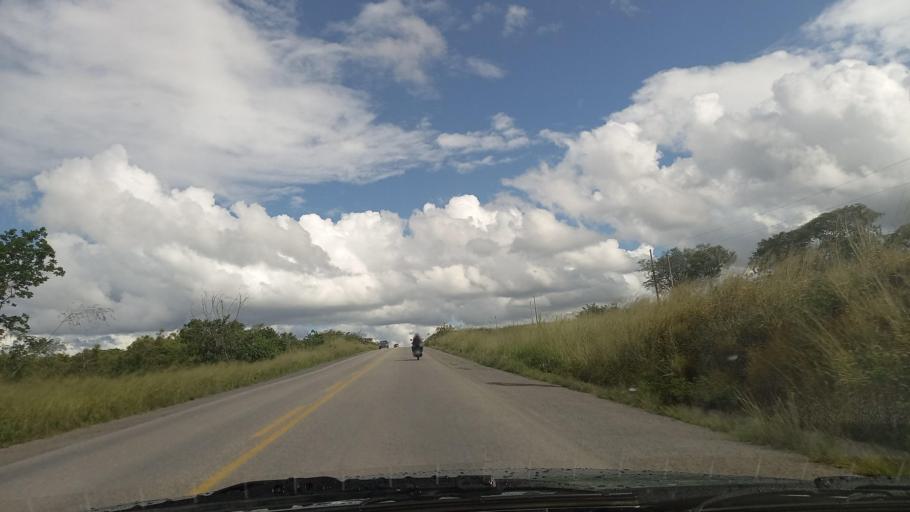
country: BR
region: Pernambuco
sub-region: Lajedo
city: Lajedo
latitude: -8.5871
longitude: -36.2892
